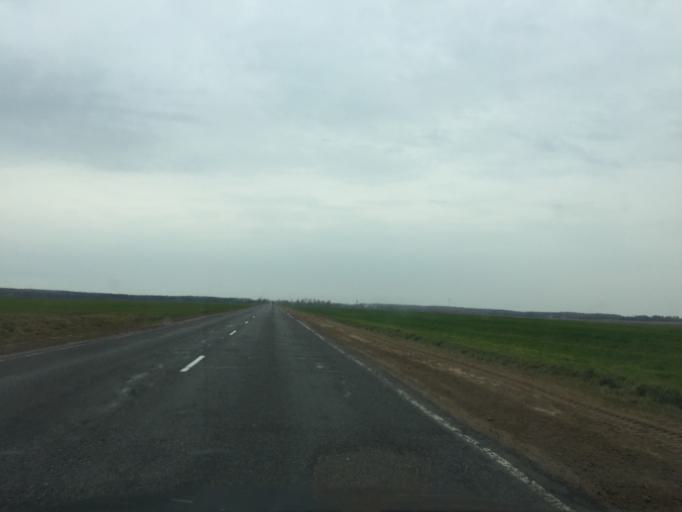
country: BY
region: Gomel
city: Dowsk
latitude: 53.1772
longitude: 30.4924
